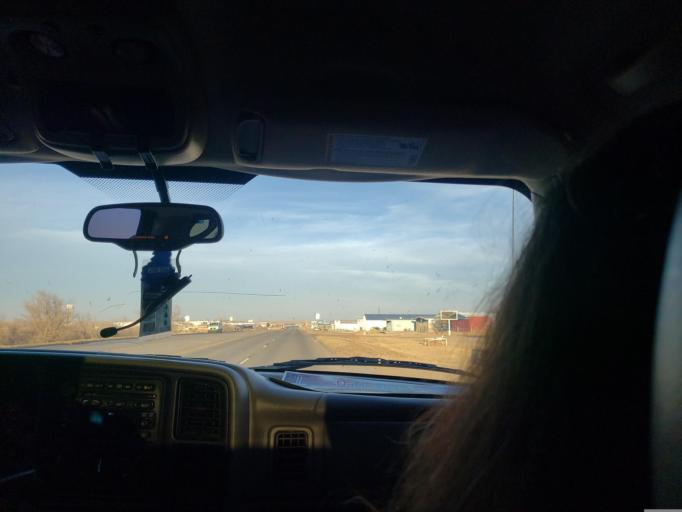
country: US
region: Oklahoma
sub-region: Texas County
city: Guymon
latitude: 36.6997
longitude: -101.4542
